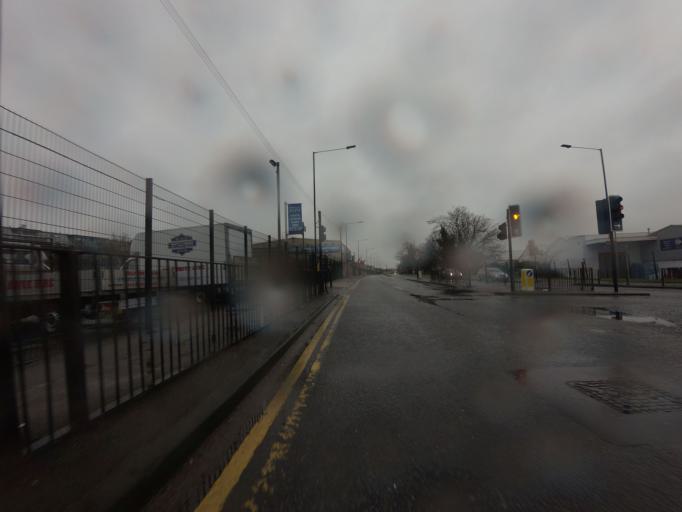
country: GB
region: England
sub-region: Hertfordshire
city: Waltham Cross
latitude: 51.6576
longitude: -0.0299
